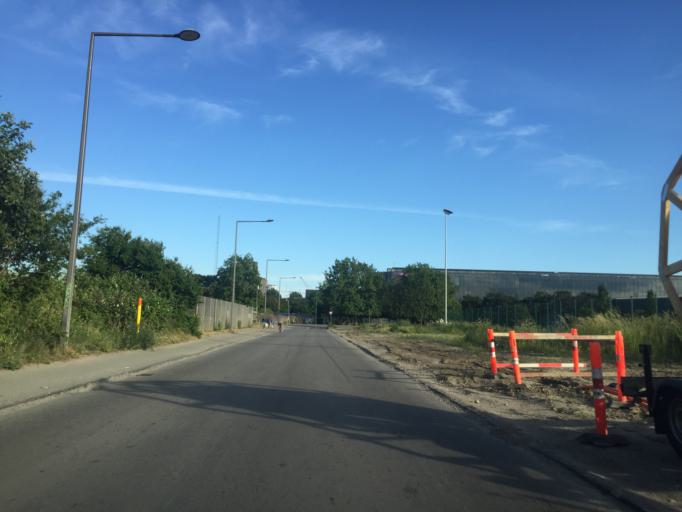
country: DK
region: Capital Region
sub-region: Kobenhavn
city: Christianshavn
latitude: 55.6704
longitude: 12.6204
